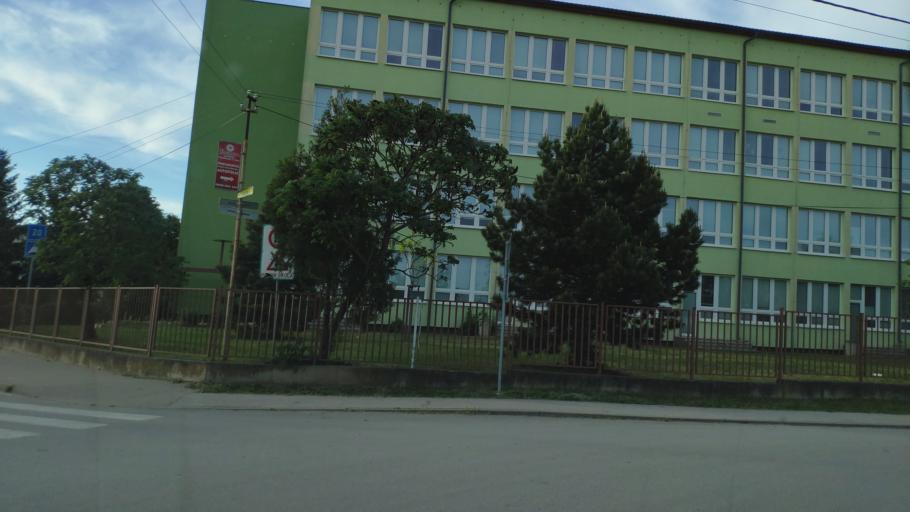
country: SK
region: Kosicky
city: Kosice
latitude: 48.6113
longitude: 21.3256
